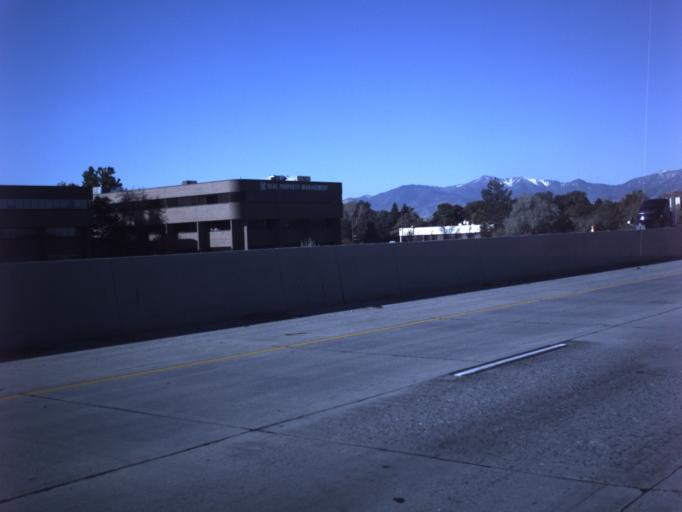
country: US
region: Utah
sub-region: Salt Lake County
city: South Salt Lake
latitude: 40.7243
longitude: -111.9318
